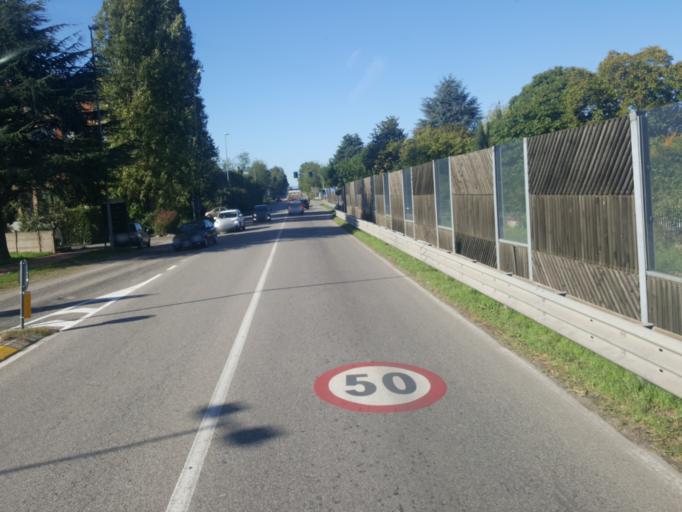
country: IT
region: Lombardy
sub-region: Citta metropolitana di Milano
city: Vittuone
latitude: 45.4849
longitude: 8.9451
